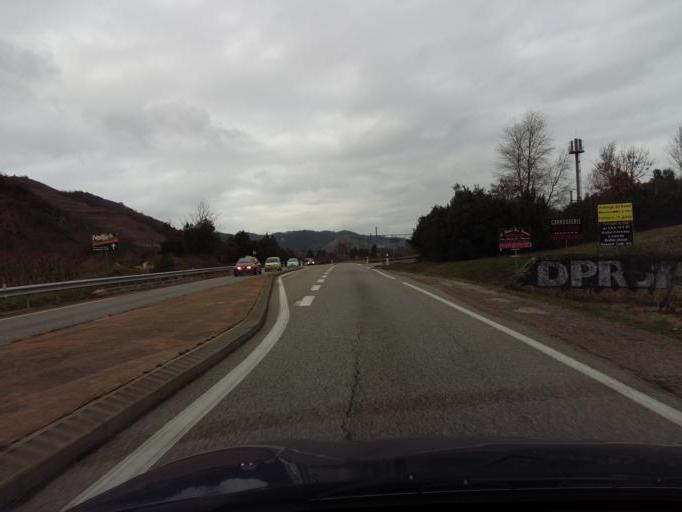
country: FR
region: Rhone-Alpes
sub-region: Departement de l'Ardeche
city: Mauves
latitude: 45.0237
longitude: 4.8318
